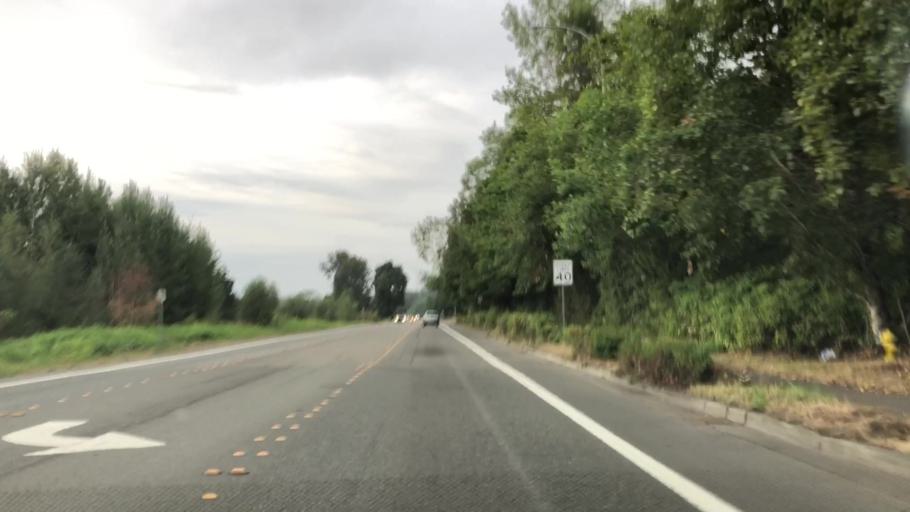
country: US
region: Washington
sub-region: King County
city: Kingsgate
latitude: 47.6998
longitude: -122.1525
